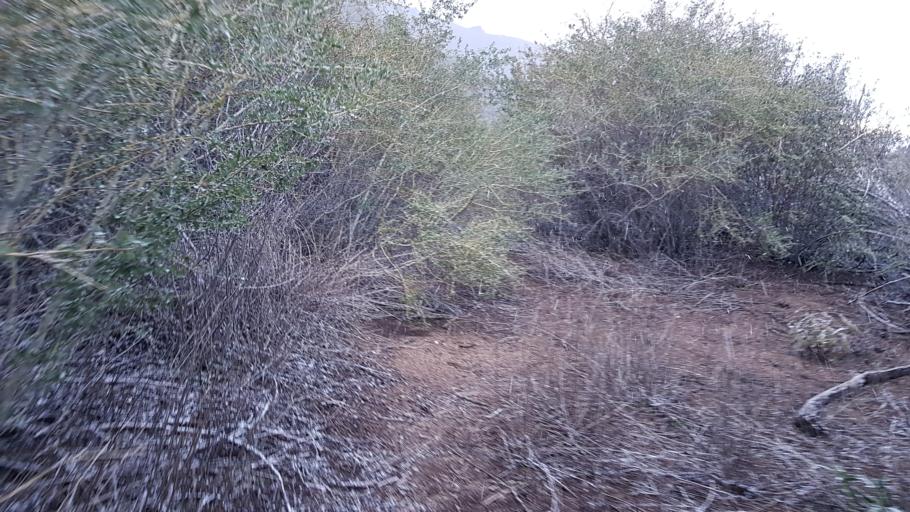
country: US
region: California
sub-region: Riverside County
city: Aguanga
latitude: 33.4000
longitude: -116.9720
